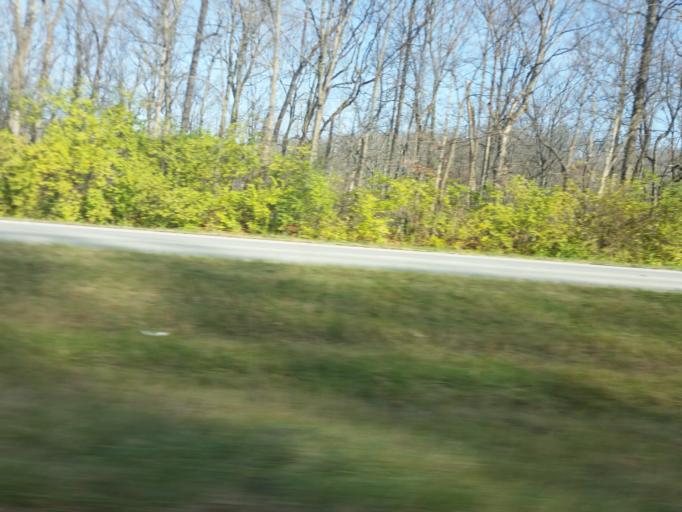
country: US
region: Ohio
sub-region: Hamilton County
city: Dunlap
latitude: 39.3008
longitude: -84.6209
